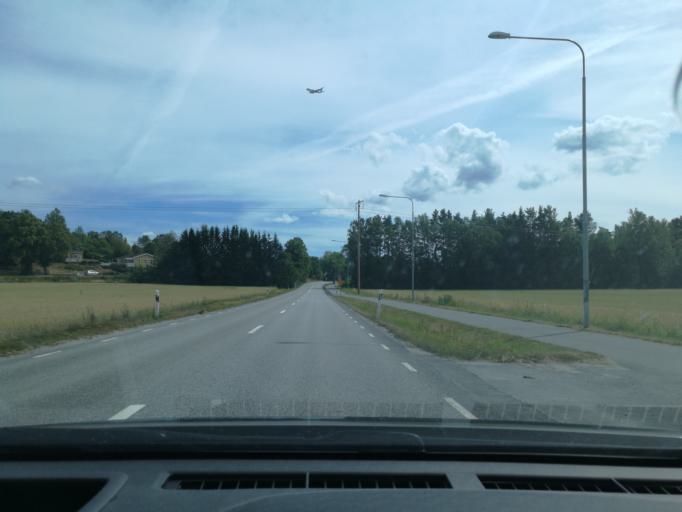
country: SE
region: Stockholm
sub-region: Sigtuna Kommun
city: Rosersberg
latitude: 59.5958
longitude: 17.8867
